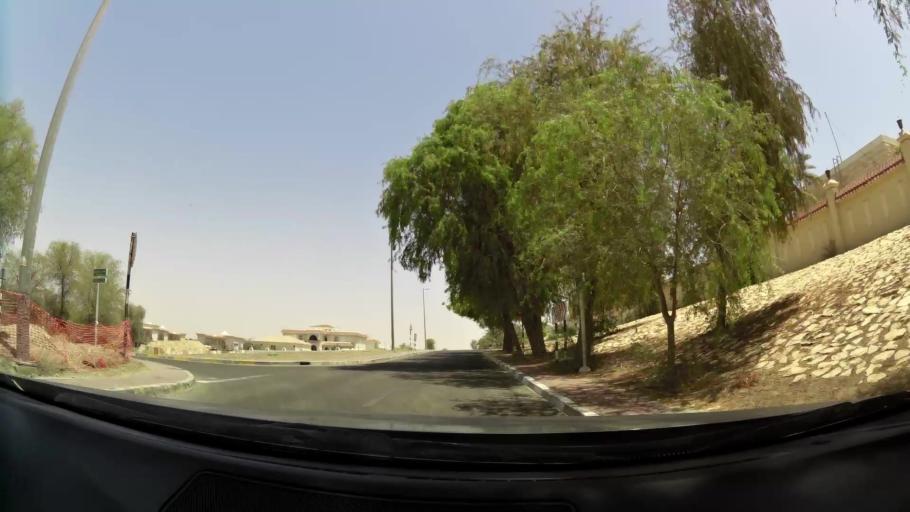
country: OM
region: Al Buraimi
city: Al Buraymi
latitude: 24.2762
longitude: 55.7480
